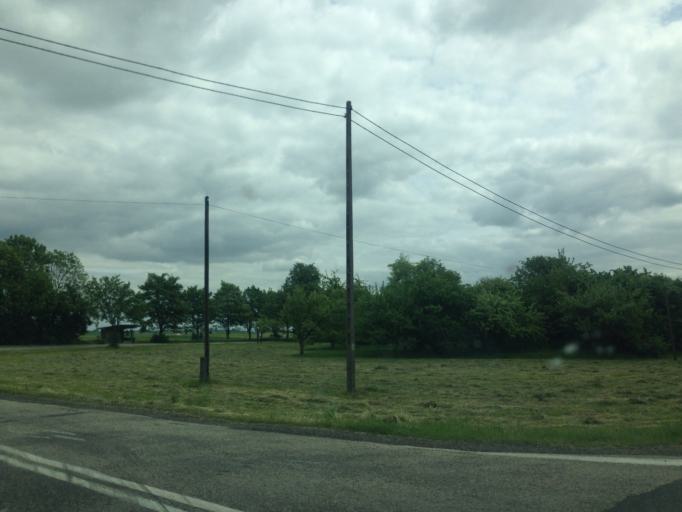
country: PL
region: Kujawsko-Pomorskie
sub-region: Powiat torunski
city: Chelmza
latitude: 53.2172
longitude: 18.5531
